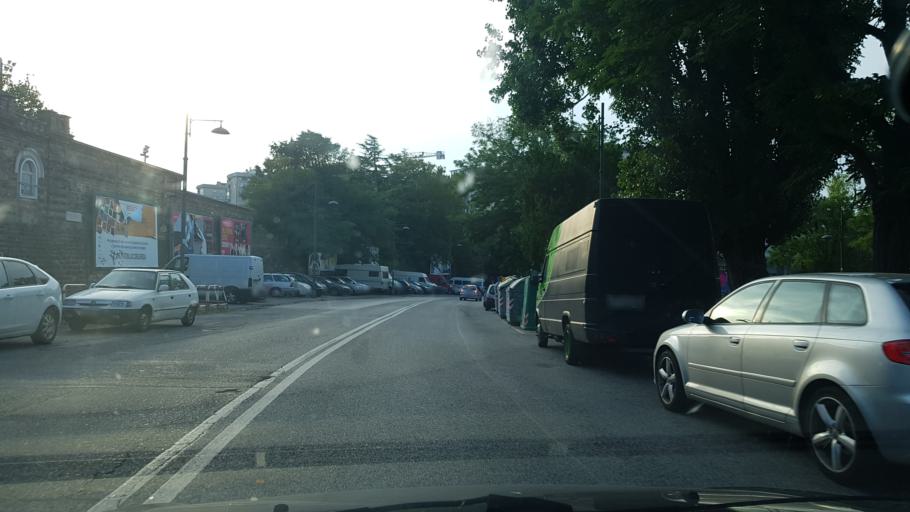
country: IT
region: Friuli Venezia Giulia
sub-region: Provincia di Trieste
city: Trieste
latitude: 45.6391
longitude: 13.7949
